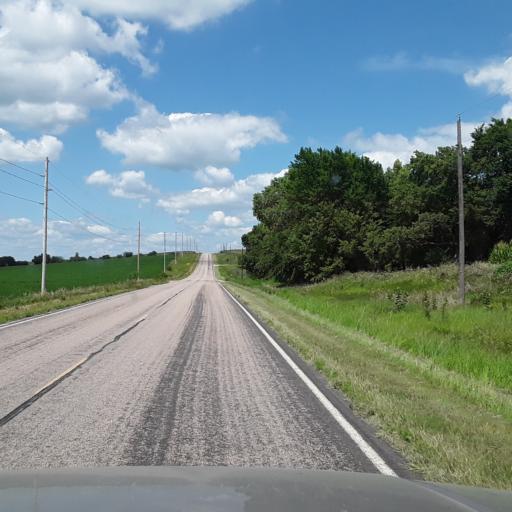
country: US
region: Nebraska
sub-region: Nance County
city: Genoa
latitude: 41.5135
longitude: -97.6960
